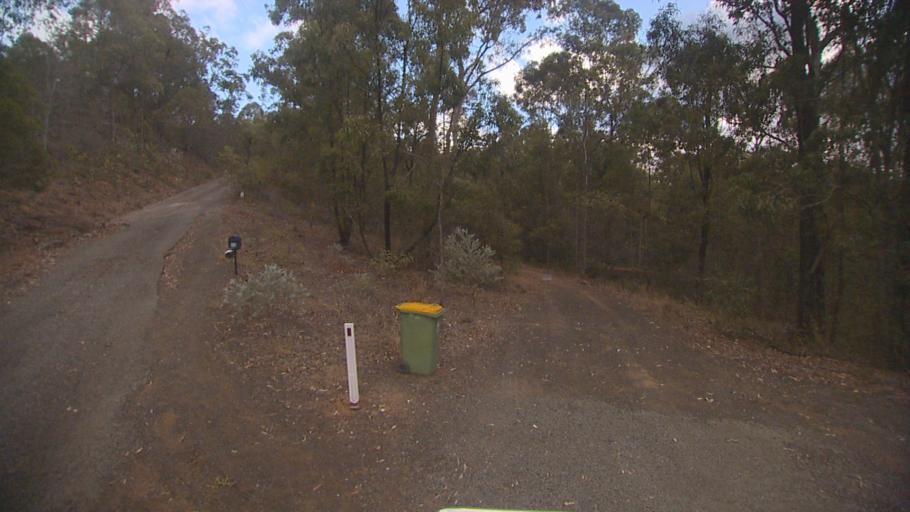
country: AU
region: Queensland
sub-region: Logan
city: Cedar Vale
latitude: -27.9346
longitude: 153.0522
